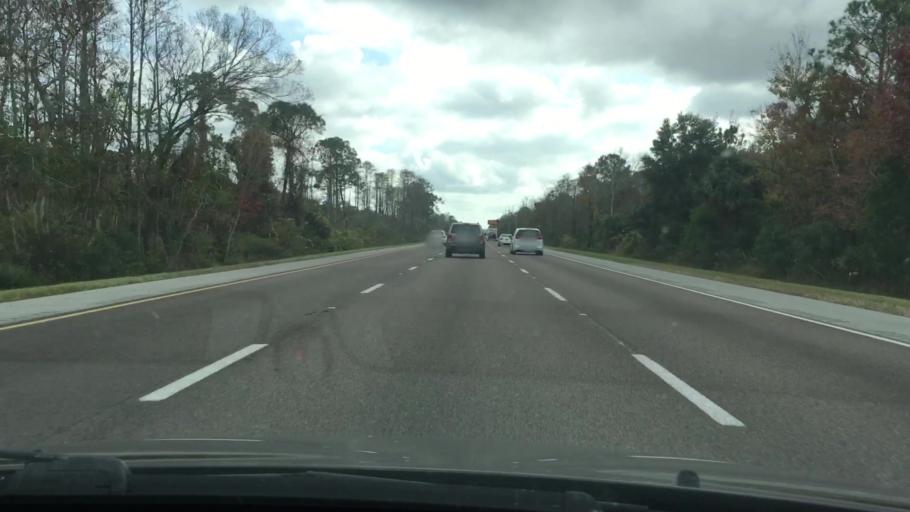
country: US
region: Florida
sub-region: Volusia County
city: Glencoe
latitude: 28.9808
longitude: -80.9673
